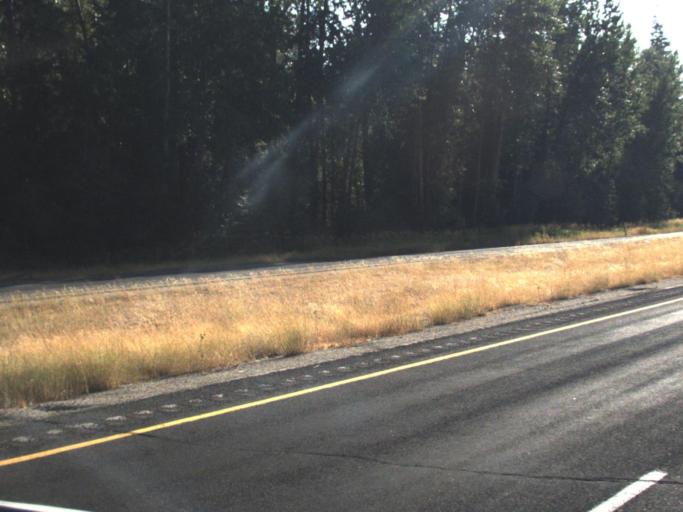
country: US
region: Washington
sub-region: Spokane County
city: Deer Park
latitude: 48.0943
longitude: -117.3205
